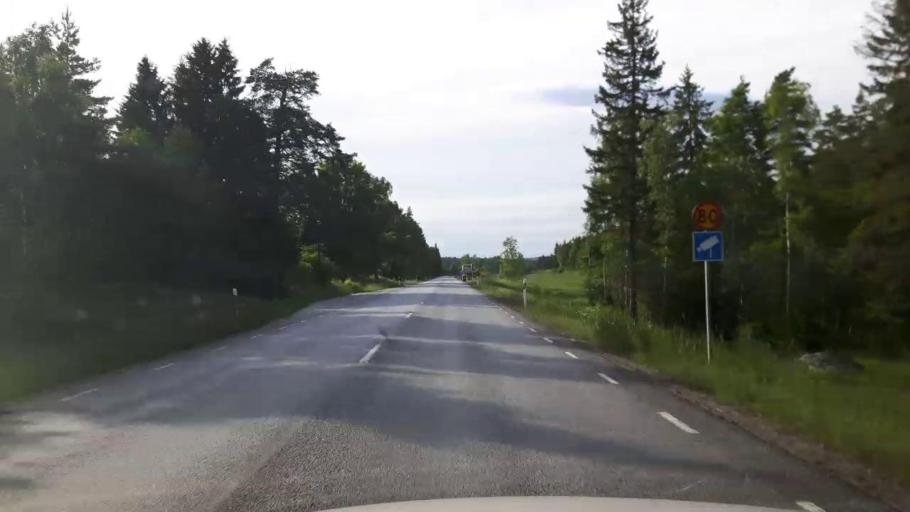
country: SE
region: Uppsala
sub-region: Habo Kommun
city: Balsta
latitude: 59.6404
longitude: 17.5732
